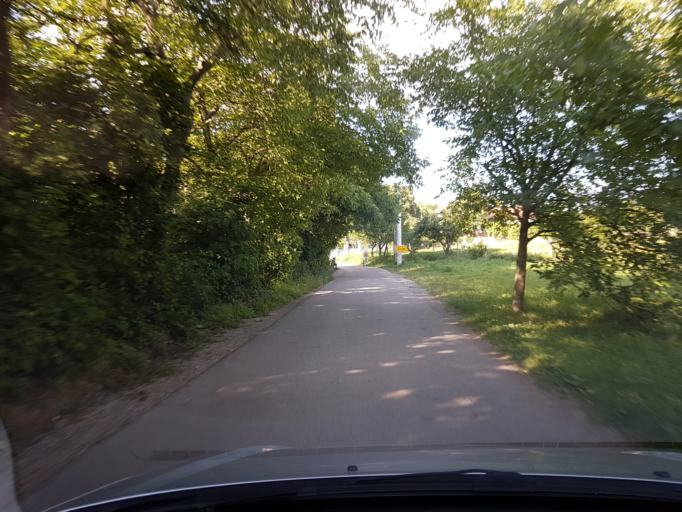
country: SI
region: Sezana
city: Sezana
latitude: 45.7066
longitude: 13.9179
